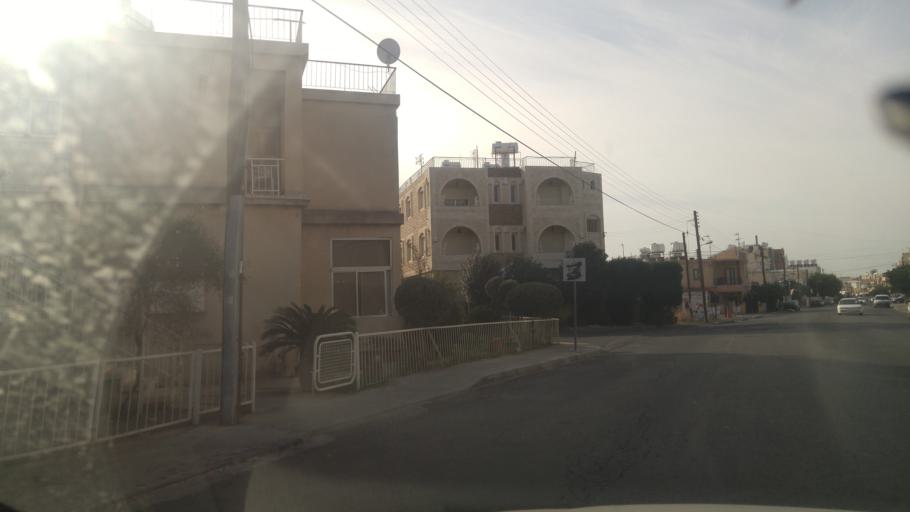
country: CY
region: Limassol
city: Limassol
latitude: 34.6722
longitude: 33.0061
